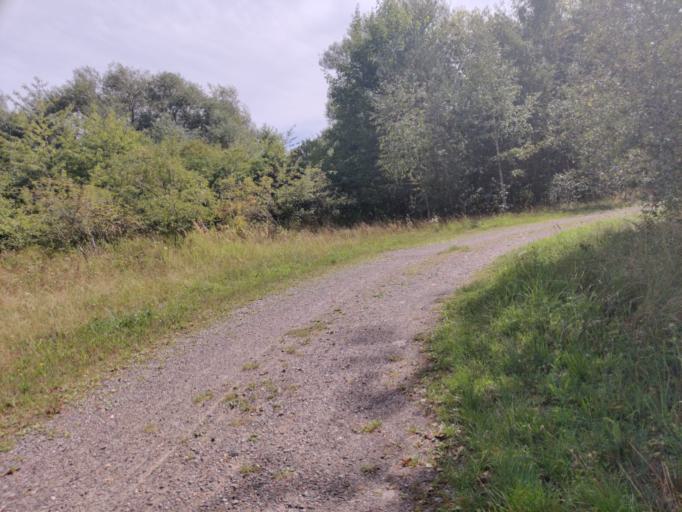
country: DE
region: Lower Saxony
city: Langelsheim
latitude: 51.9676
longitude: 10.3665
